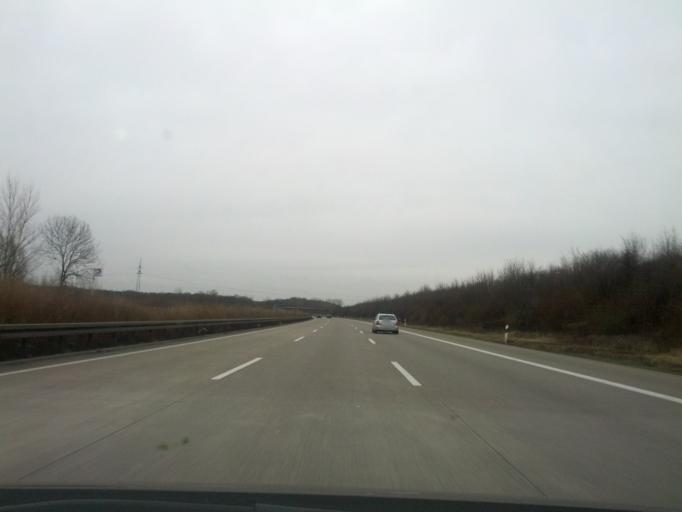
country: DE
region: Lower Saxony
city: Laatzen
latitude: 52.3323
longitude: 9.8635
